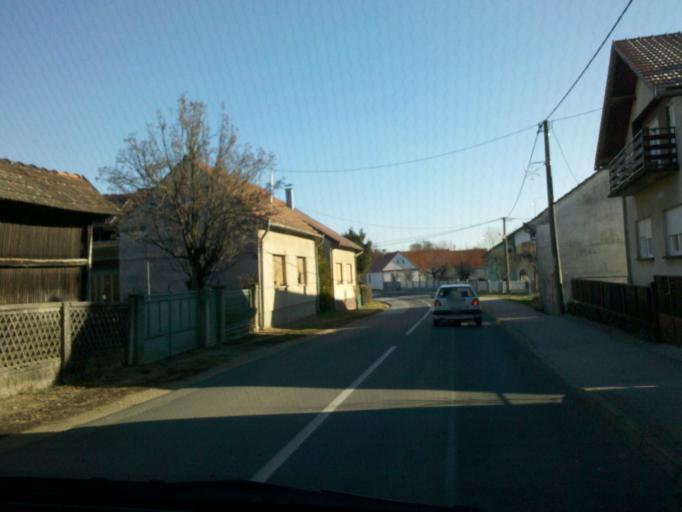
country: HR
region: Medimurska
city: Kotoriba
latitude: 46.3300
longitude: 16.7889
